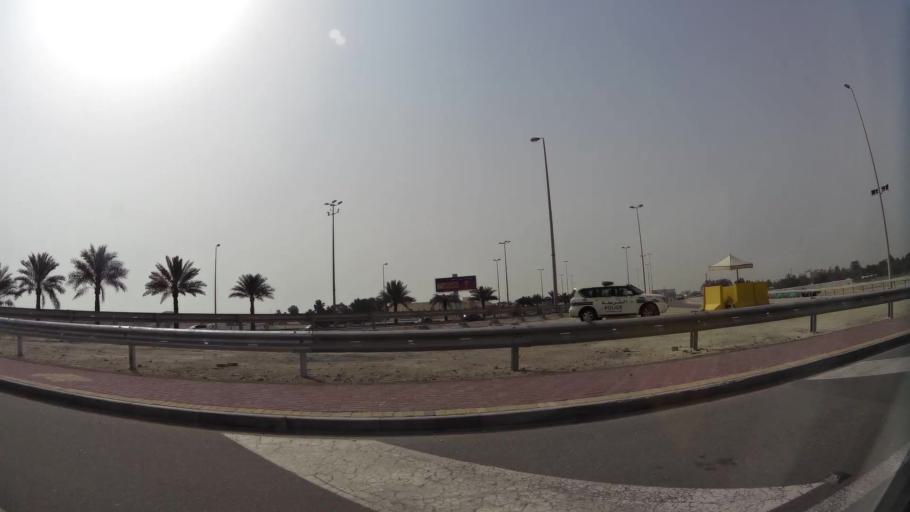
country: BH
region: Manama
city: Jidd Hafs
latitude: 26.2234
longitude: 50.5226
